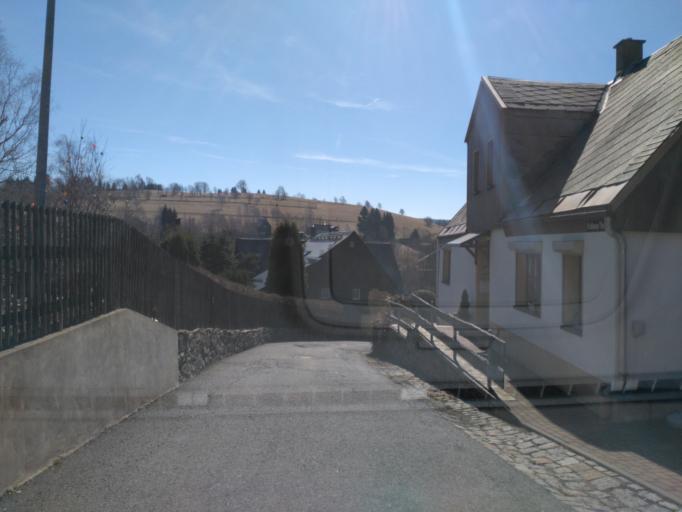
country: CZ
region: Ustecky
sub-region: Okres Chomutov
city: Vejprty
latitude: 50.4905
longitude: 13.0223
